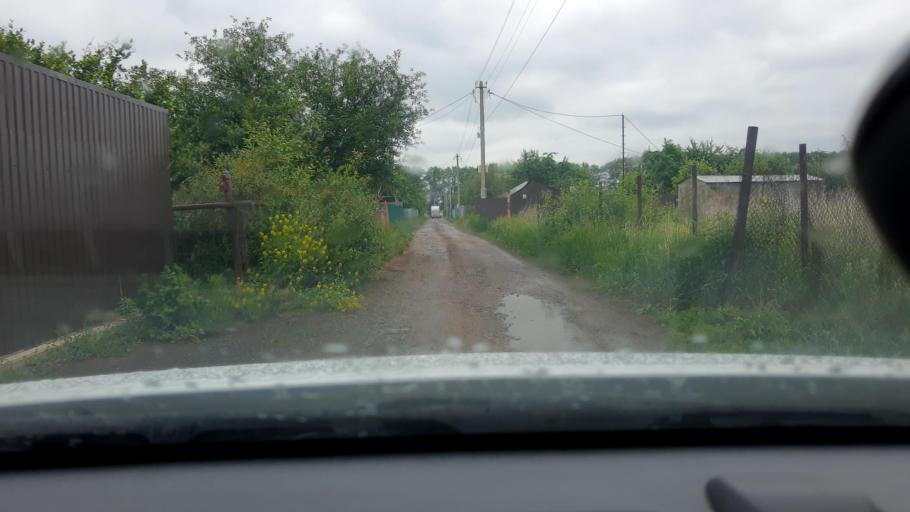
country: RU
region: Bashkortostan
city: Kabakovo
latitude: 54.4695
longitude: 55.9391
